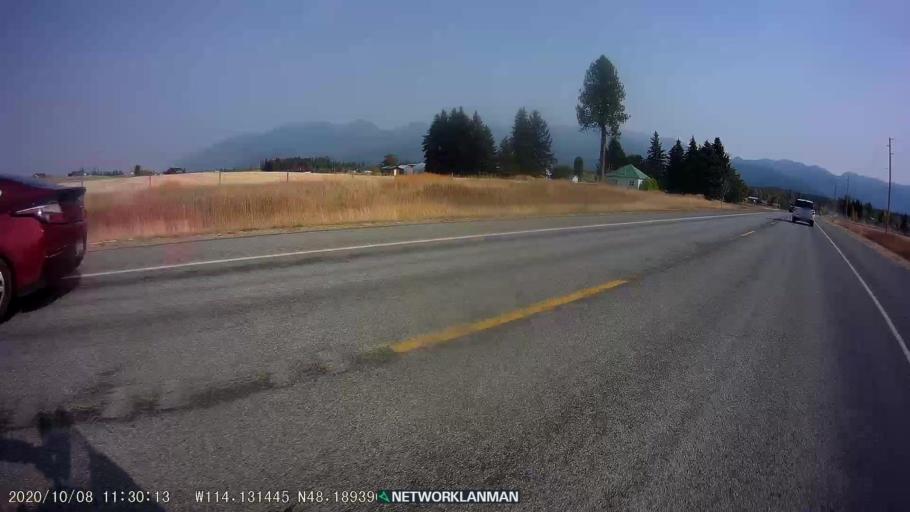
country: US
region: Montana
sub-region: Flathead County
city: Bigfork
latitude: 48.1899
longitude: -114.1314
